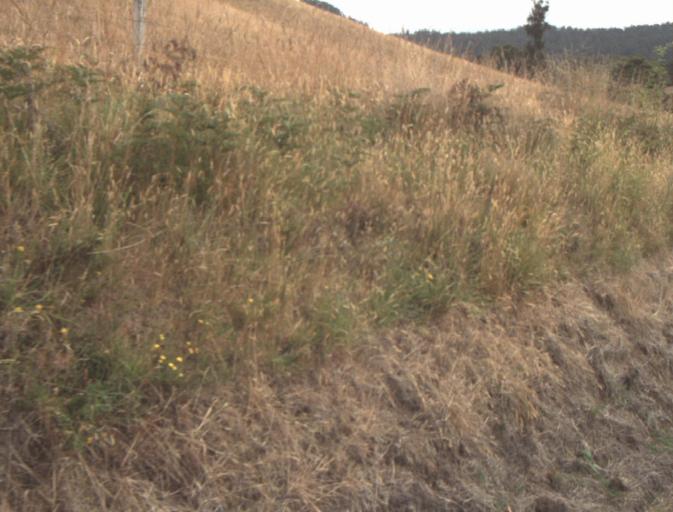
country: AU
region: Tasmania
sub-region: Dorset
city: Scottsdale
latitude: -41.4641
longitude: 147.5941
